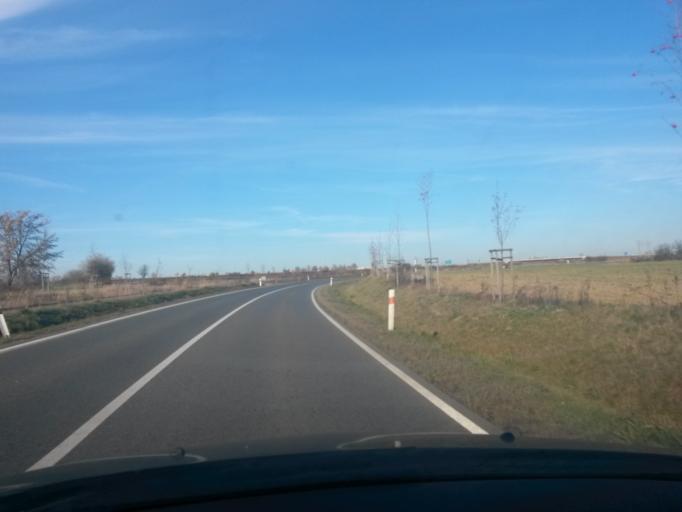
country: CZ
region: Central Bohemia
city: Jesenice
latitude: 49.9563
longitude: 14.5178
